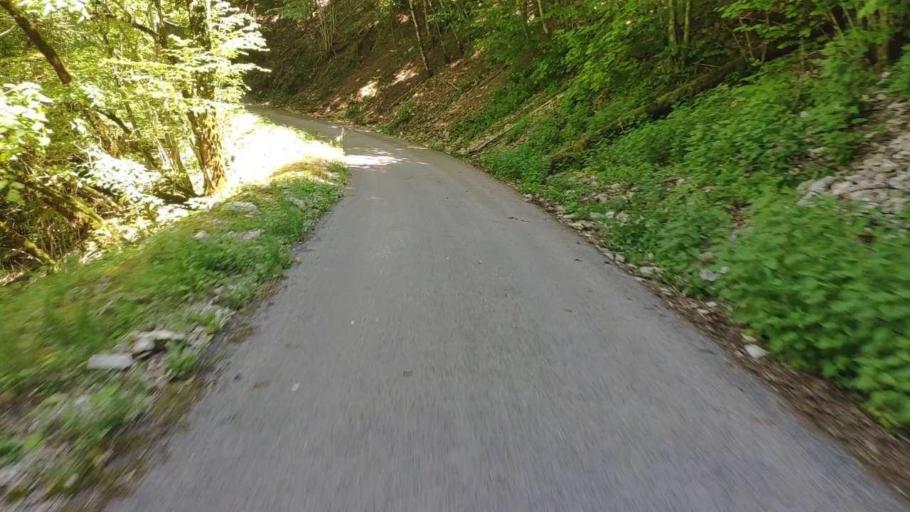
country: FR
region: Franche-Comte
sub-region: Departement du Jura
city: Poligny
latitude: 46.7462
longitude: 5.6832
